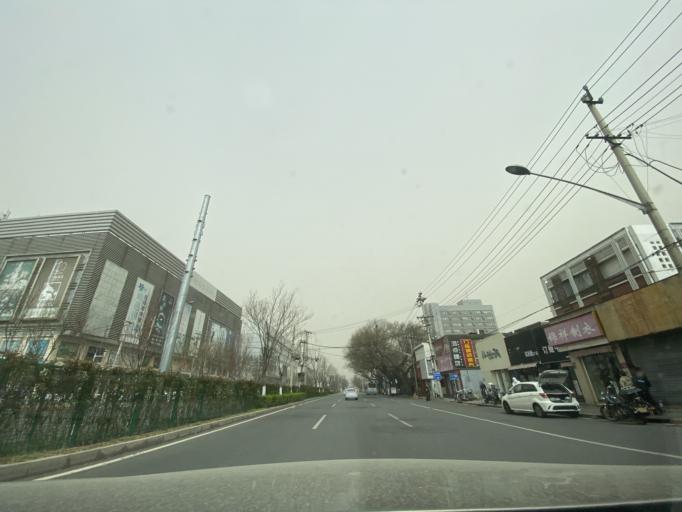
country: CN
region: Beijing
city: Jinrongjie
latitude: 39.9406
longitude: 116.3663
